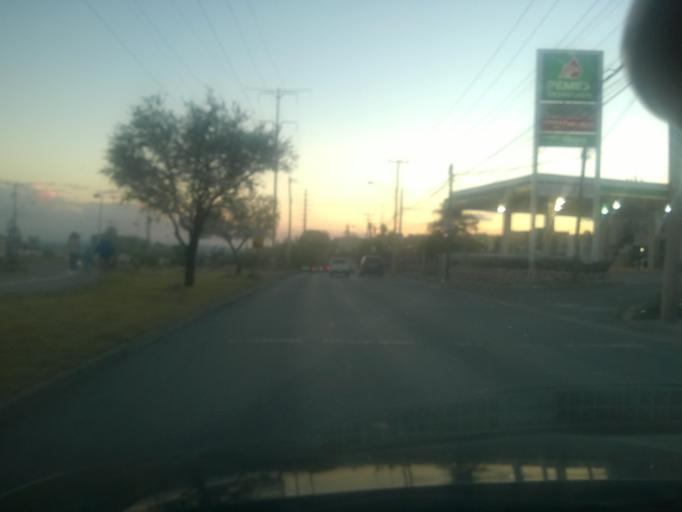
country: MX
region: Guanajuato
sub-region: Leon
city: Ejido la Joya
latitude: 21.1117
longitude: -101.7112
